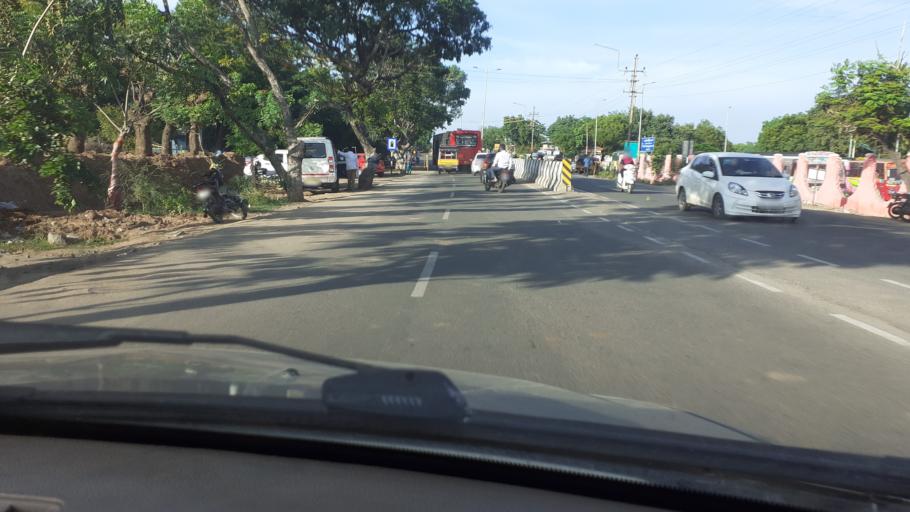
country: IN
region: Tamil Nadu
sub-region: Tirunelveli Kattabo
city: Tirunelveli
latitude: 8.7047
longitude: 77.7301
